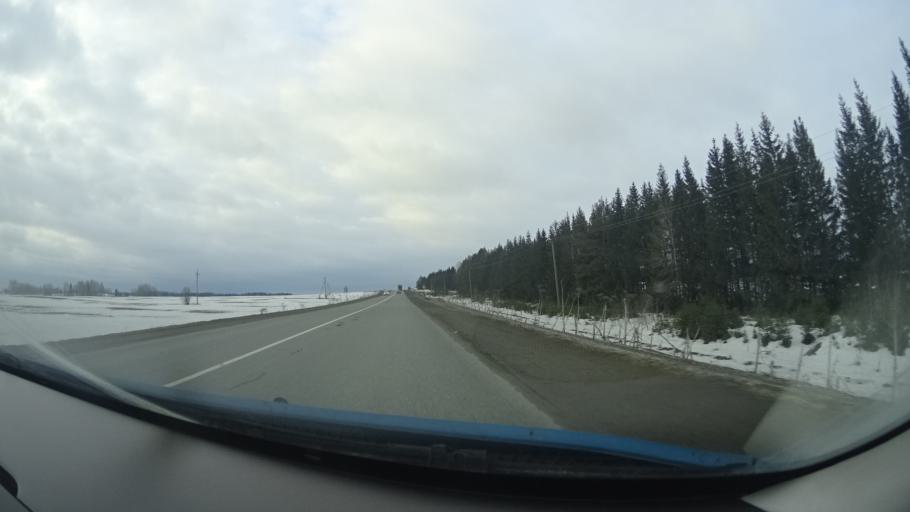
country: RU
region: Perm
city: Osa
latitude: 57.2722
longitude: 55.5702
